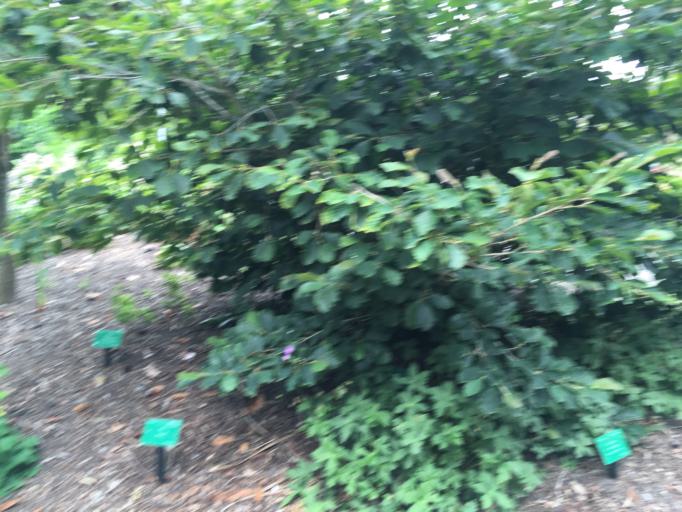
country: NZ
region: Canterbury
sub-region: Christchurch City
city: Christchurch
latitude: -43.5293
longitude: 172.6211
